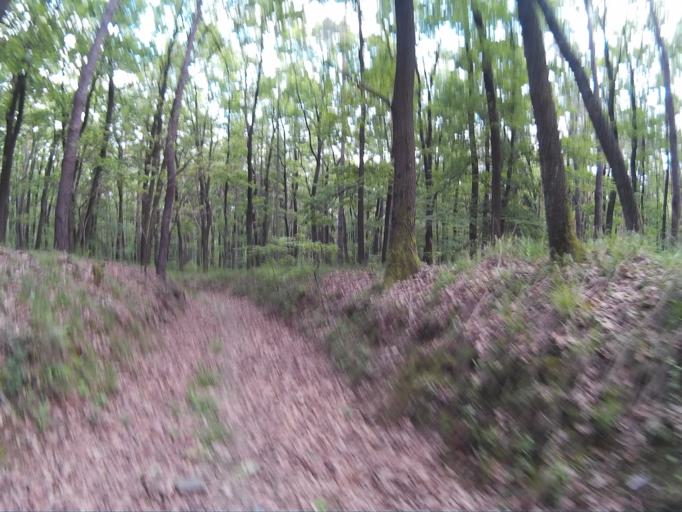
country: HU
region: Vas
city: Koszeg
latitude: 47.3728
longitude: 16.5076
